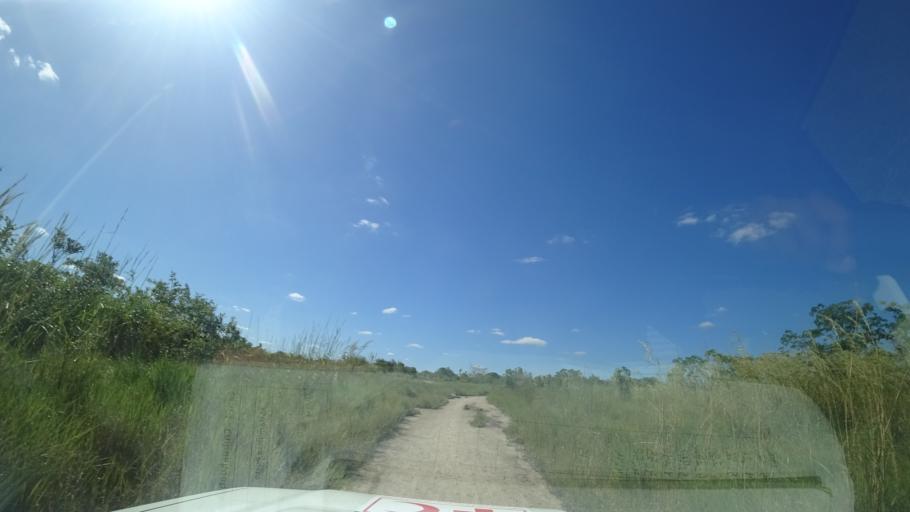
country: MZ
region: Sofala
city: Dondo
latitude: -19.4780
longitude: 34.6270
